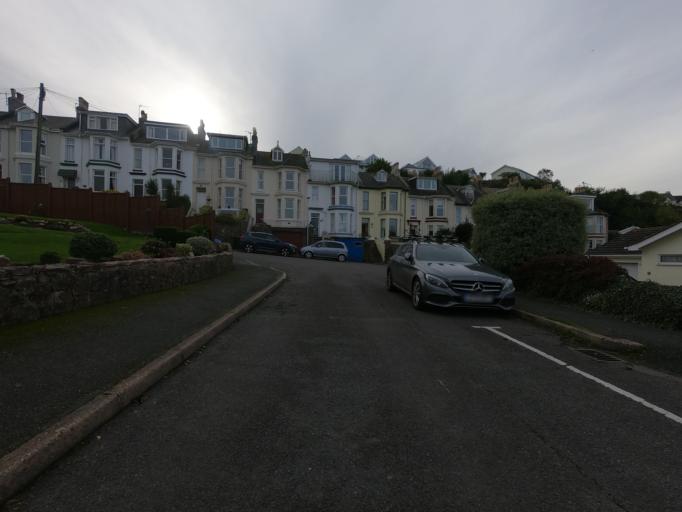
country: GB
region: England
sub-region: Borough of Torbay
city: Brixham
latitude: 50.3956
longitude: -3.5065
